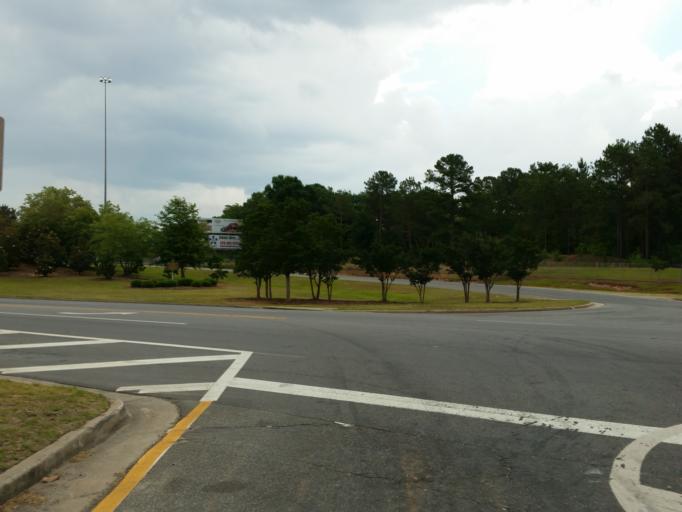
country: US
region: Georgia
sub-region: Tift County
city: Tifton
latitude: 31.4778
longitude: -83.5197
